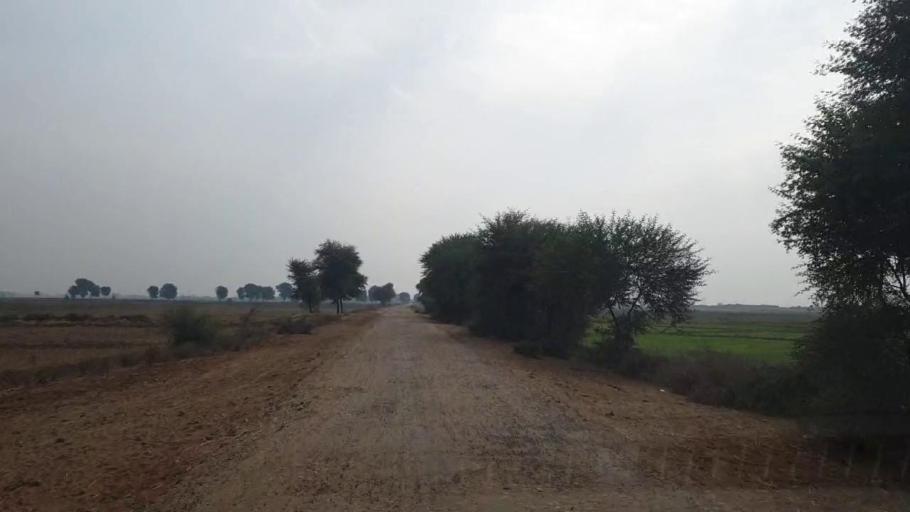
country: PK
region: Sindh
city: Sann
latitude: 26.0227
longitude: 68.1431
